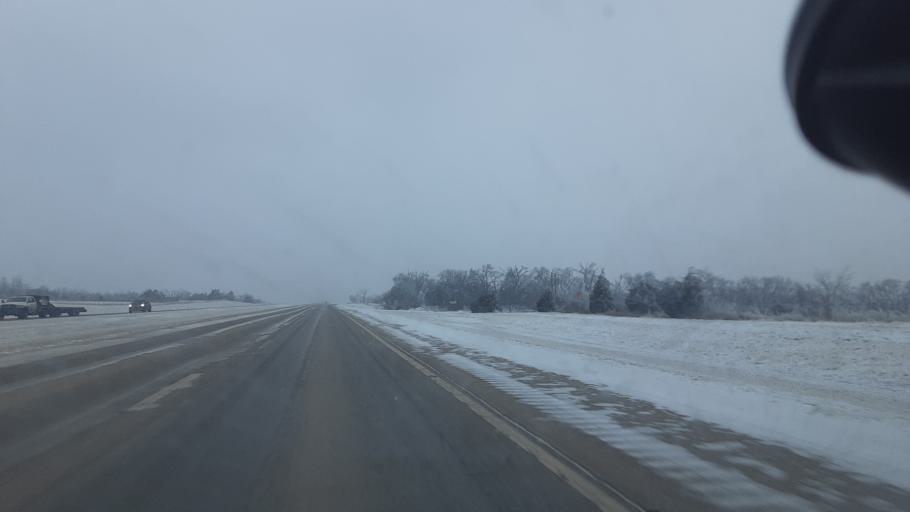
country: US
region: Oklahoma
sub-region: Logan County
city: Guthrie
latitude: 35.9028
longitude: -97.3440
